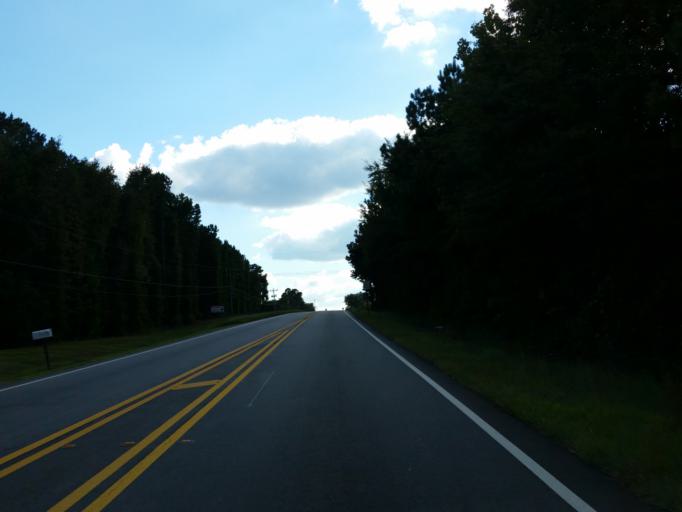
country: US
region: Georgia
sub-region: Butts County
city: Jackson
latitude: 33.1989
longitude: -84.0671
